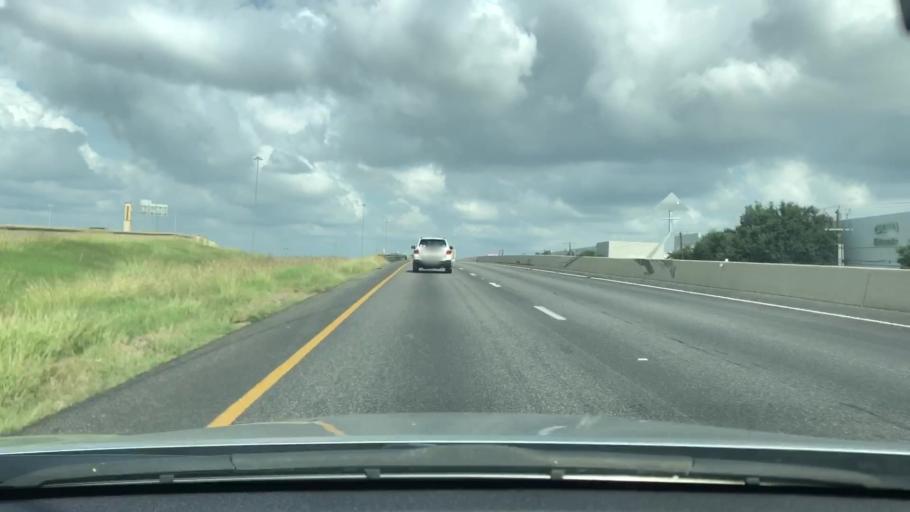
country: US
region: Texas
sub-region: Bexar County
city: Kirby
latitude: 29.4708
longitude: -98.4041
